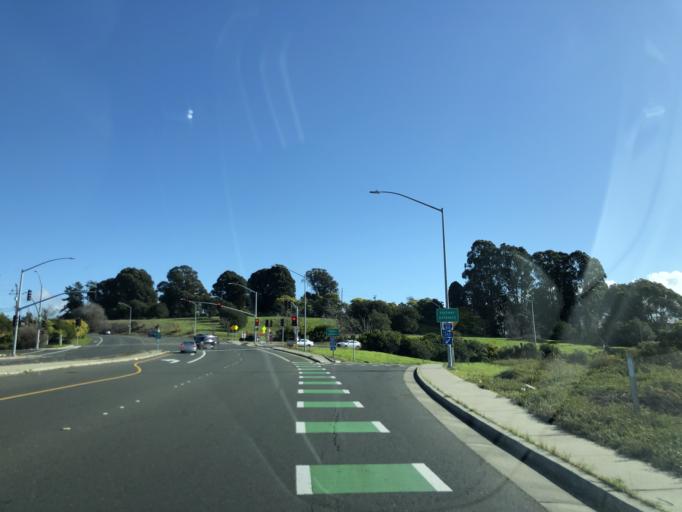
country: US
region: California
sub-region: Contra Costa County
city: Rollingwood
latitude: 37.9761
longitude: -122.3179
